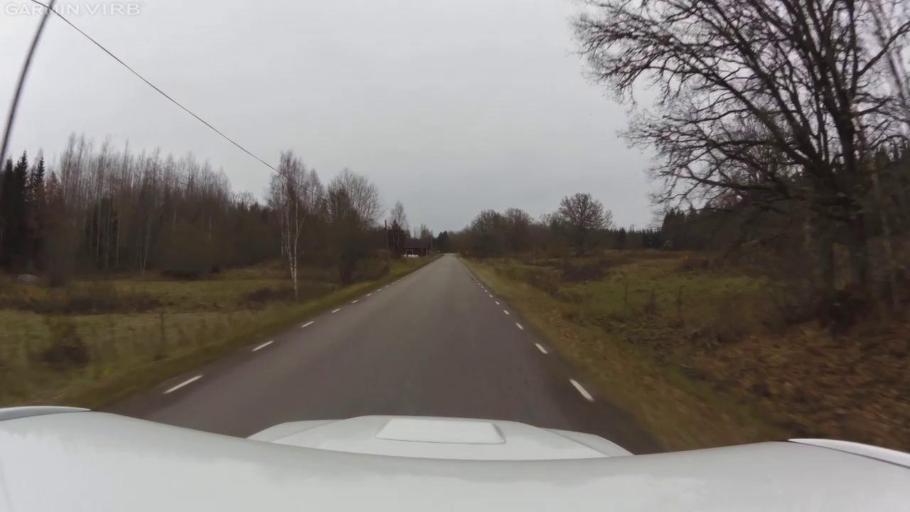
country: SE
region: OEstergoetland
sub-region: Linkopings Kommun
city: Vikingstad
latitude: 58.2550
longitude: 15.3834
